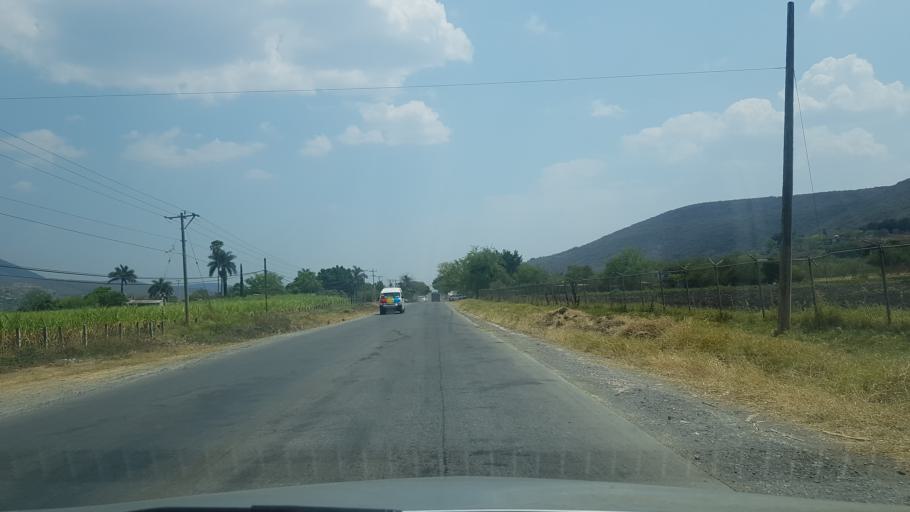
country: MX
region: Morelos
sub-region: Tlaltizapan de Zapata
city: Colonia Palo Prieto (Chipitongo)
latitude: 18.7274
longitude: -99.1236
